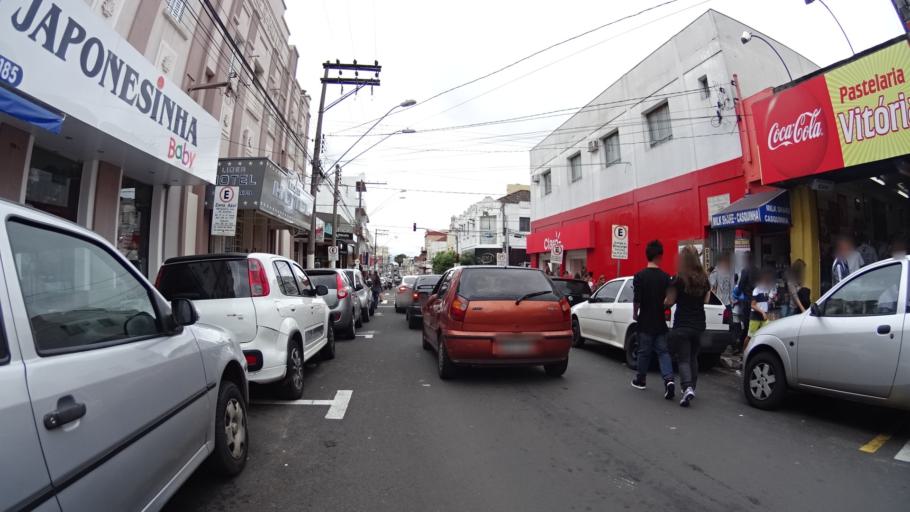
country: BR
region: Sao Paulo
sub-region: Marilia
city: Marilia
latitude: -22.2180
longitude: -49.9499
